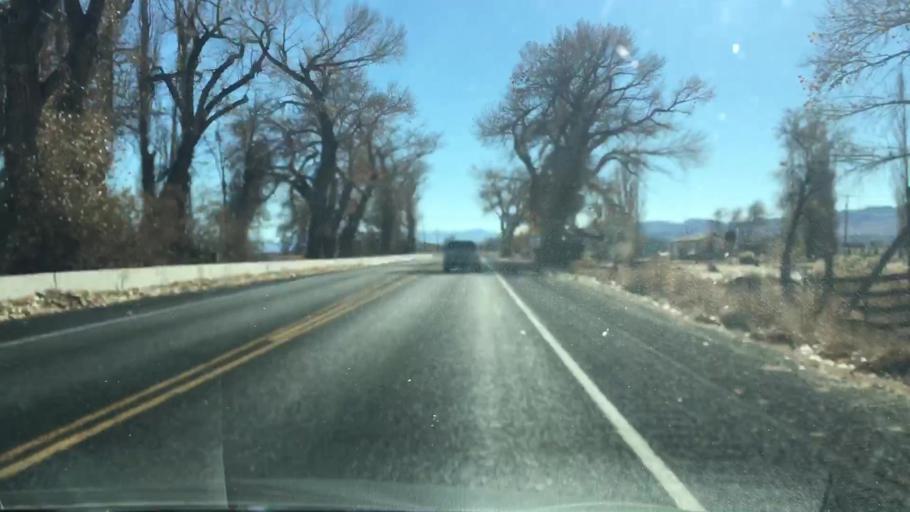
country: US
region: Nevada
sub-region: Lyon County
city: Yerington
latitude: 39.0502
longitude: -119.1815
